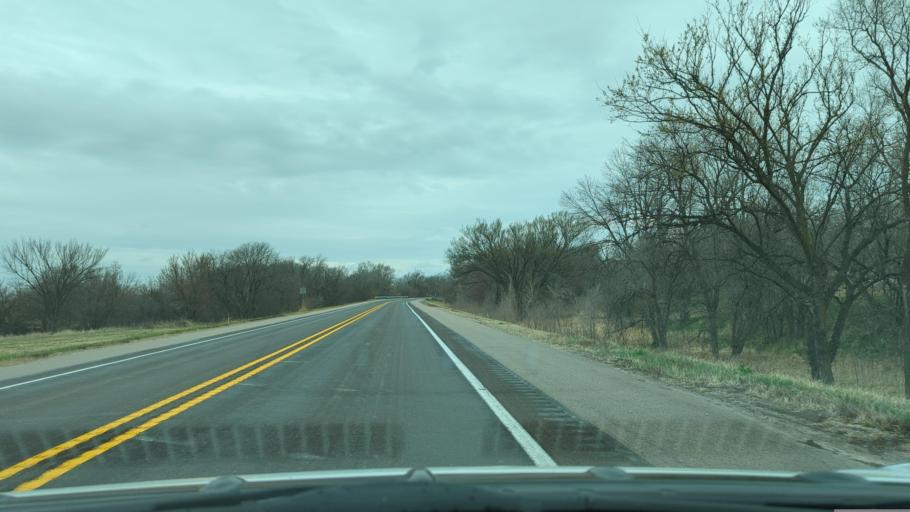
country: US
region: Nebraska
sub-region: Lancaster County
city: Waverly
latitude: 40.9534
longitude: -96.4506
